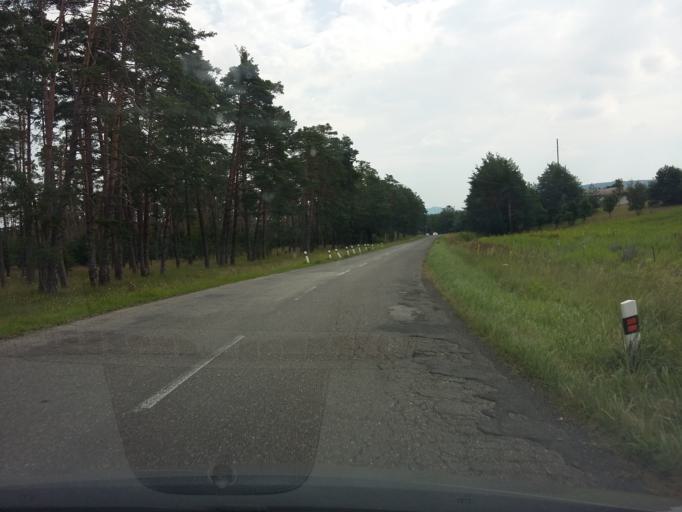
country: SK
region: Bratislavsky
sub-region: Okres Malacky
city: Malacky
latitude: 48.4604
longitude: 17.1429
